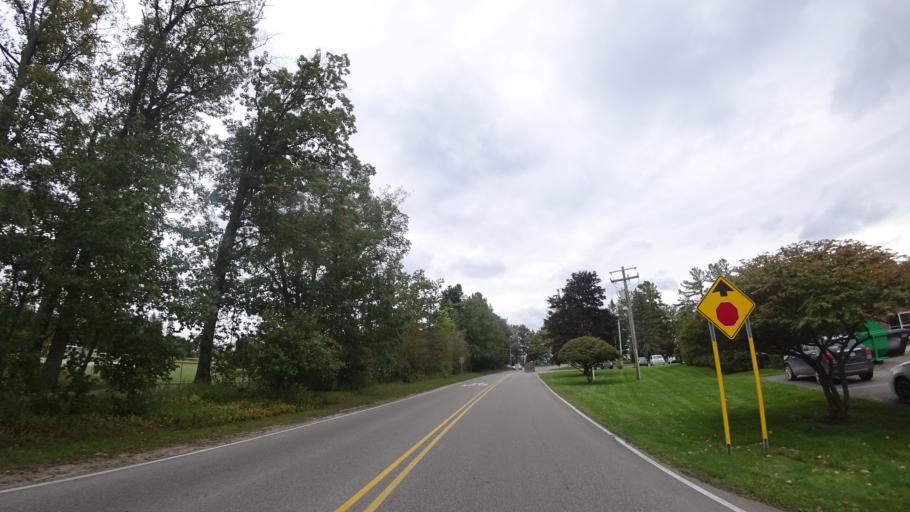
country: US
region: Michigan
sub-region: Emmet County
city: Harbor Springs
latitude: 45.4337
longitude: -84.9712
